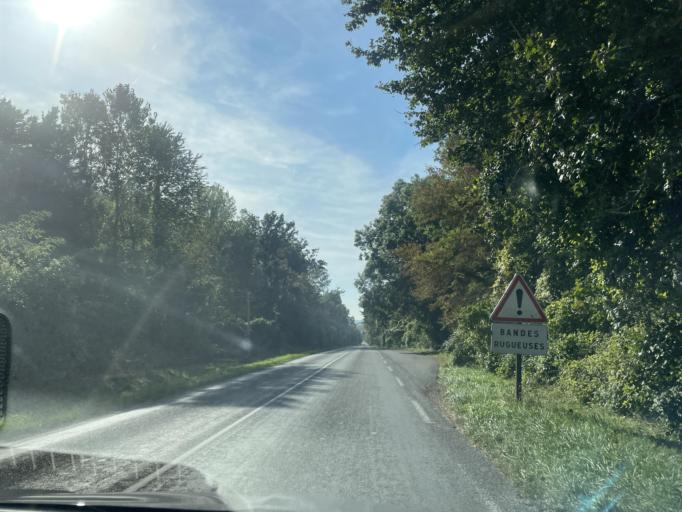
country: FR
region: Ile-de-France
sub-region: Departement de Seine-et-Marne
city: Coulommiers
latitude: 48.8469
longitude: 3.0894
